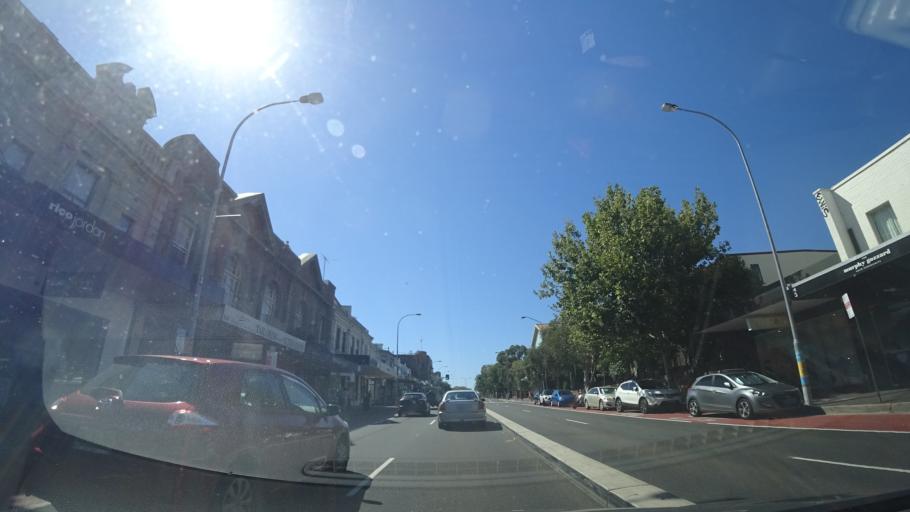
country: AU
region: New South Wales
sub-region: Woollahra
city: Paddington
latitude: -33.8877
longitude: 151.2311
